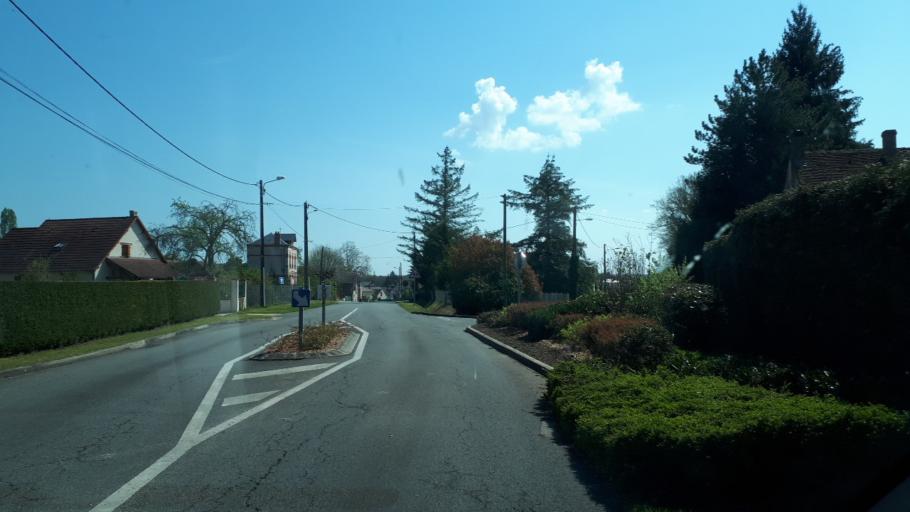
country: FR
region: Centre
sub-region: Departement du Cher
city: Neuvy-sur-Barangeon
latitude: 47.3161
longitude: 2.2494
